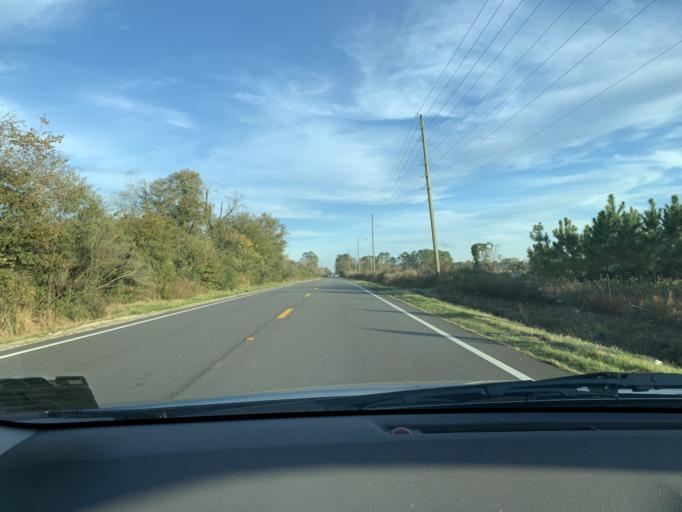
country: US
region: Georgia
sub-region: Irwin County
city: Ocilla
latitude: 31.5878
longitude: -83.0857
